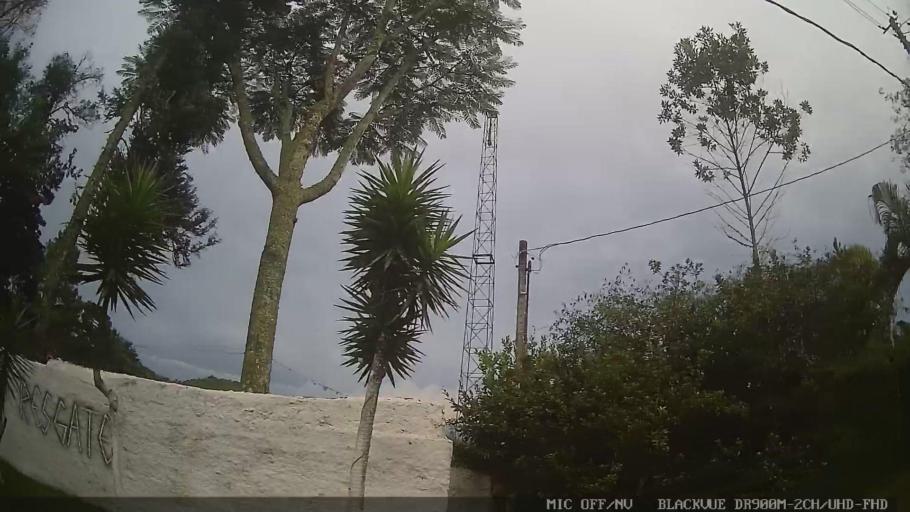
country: BR
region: Sao Paulo
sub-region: Rio Grande Da Serra
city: Rio Grande da Serra
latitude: -23.6931
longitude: -46.3242
